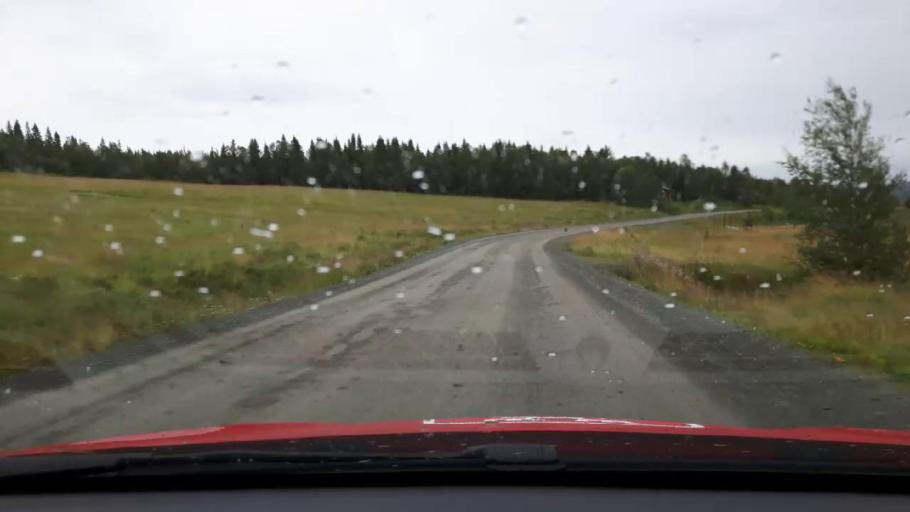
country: SE
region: Jaemtland
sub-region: Are Kommun
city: Are
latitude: 63.4616
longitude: 12.6329
